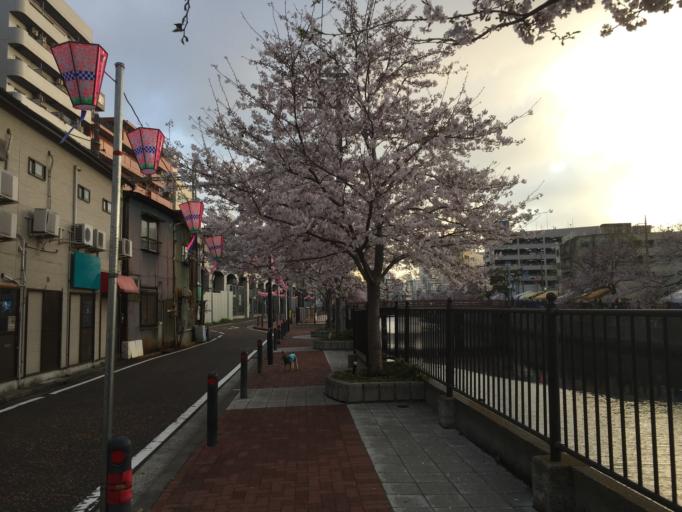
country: JP
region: Kanagawa
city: Yokohama
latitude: 35.4428
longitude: 139.6264
